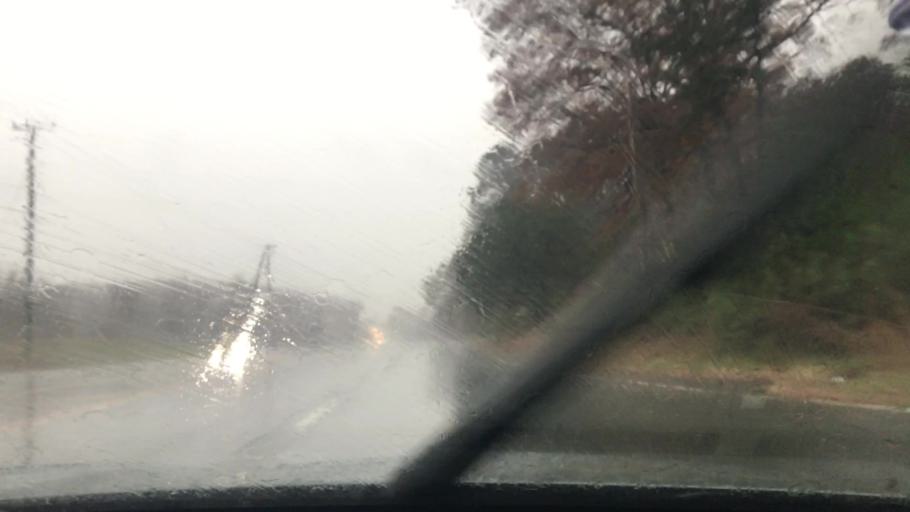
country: US
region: Virginia
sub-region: Stafford County
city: Aquia Harbour
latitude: 38.4721
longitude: -77.3976
